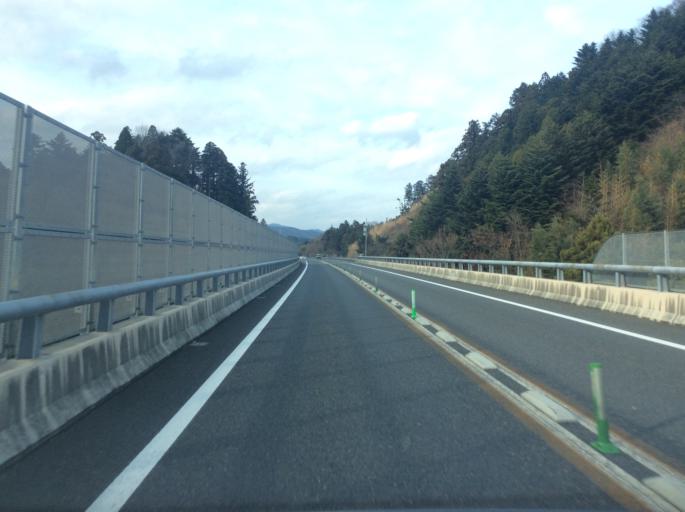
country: JP
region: Fukushima
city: Iwaki
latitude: 37.2041
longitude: 140.9846
